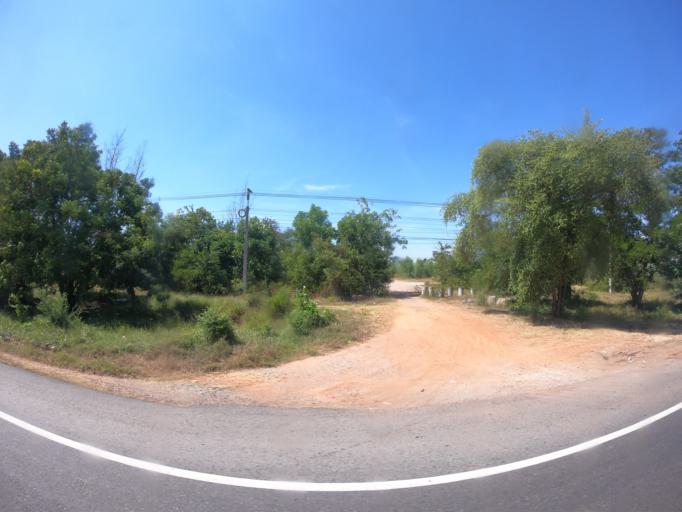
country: TH
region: Khon Kaen
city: Ban Phai
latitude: 16.0165
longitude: 102.7067
